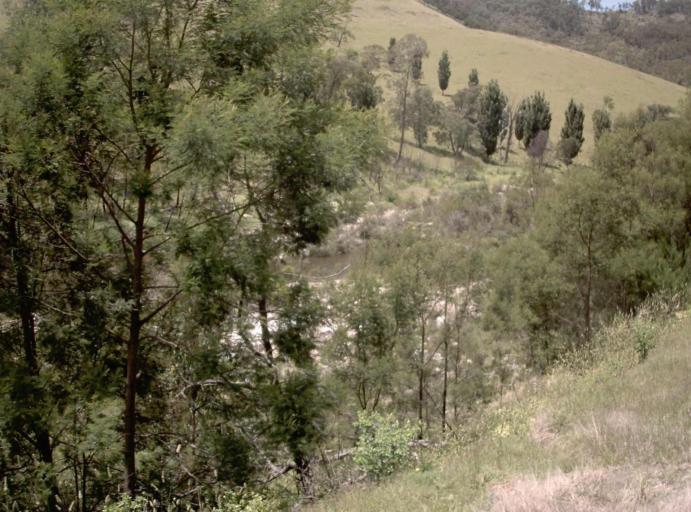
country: AU
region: Victoria
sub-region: East Gippsland
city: Bairnsdale
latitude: -37.5163
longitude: 147.8470
